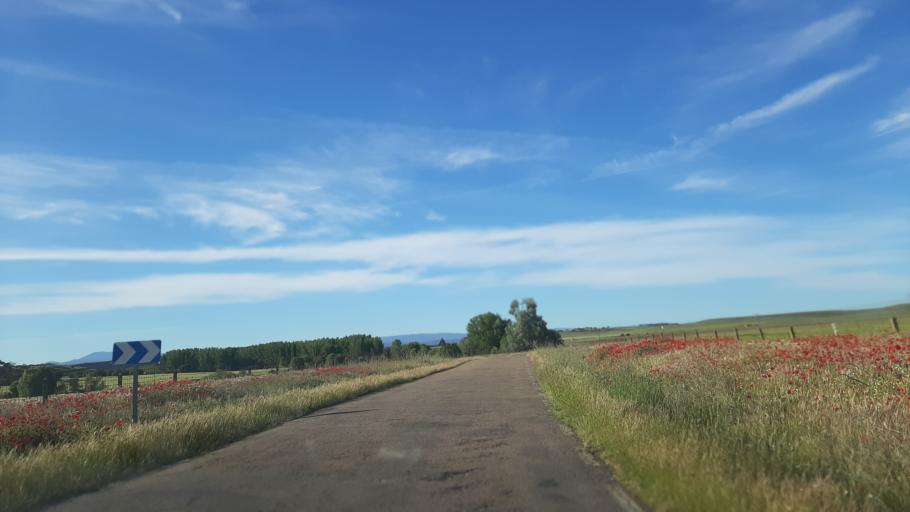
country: ES
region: Castille and Leon
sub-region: Provincia de Salamanca
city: Gajates
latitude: 40.7963
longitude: -5.3729
